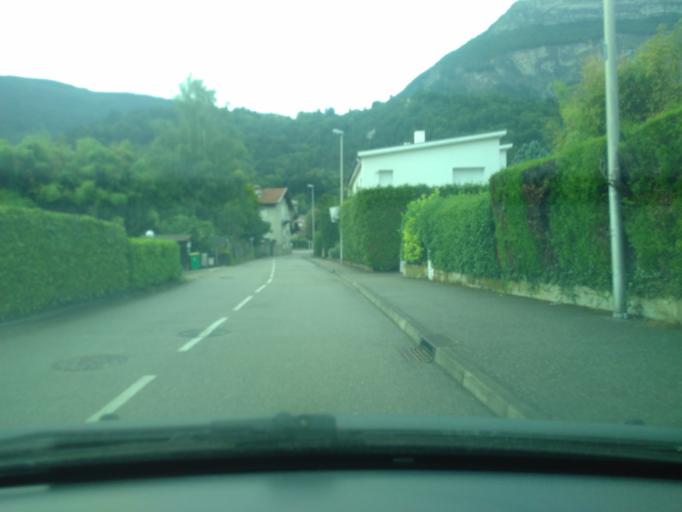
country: FR
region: Rhone-Alpes
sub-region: Departement de l'Isere
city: Corenc
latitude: 45.2112
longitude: 5.7667
